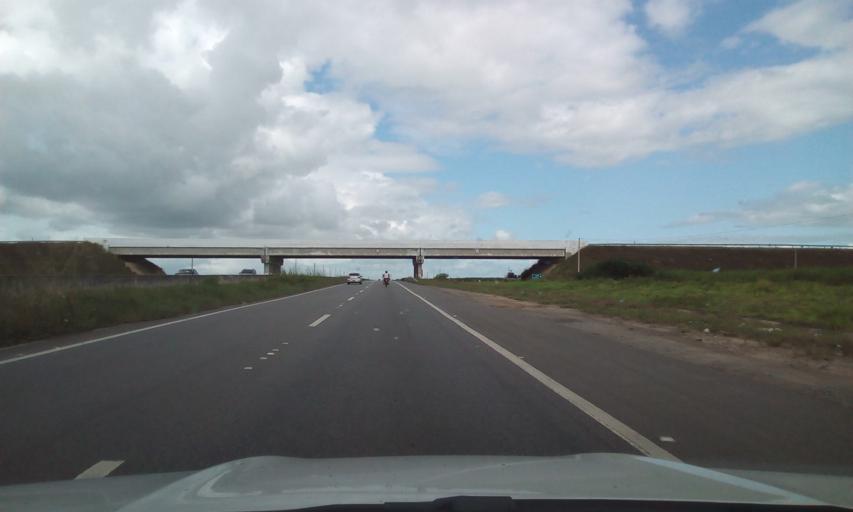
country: BR
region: Pernambuco
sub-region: Goiana
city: Goiana
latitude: -7.6115
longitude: -34.9748
